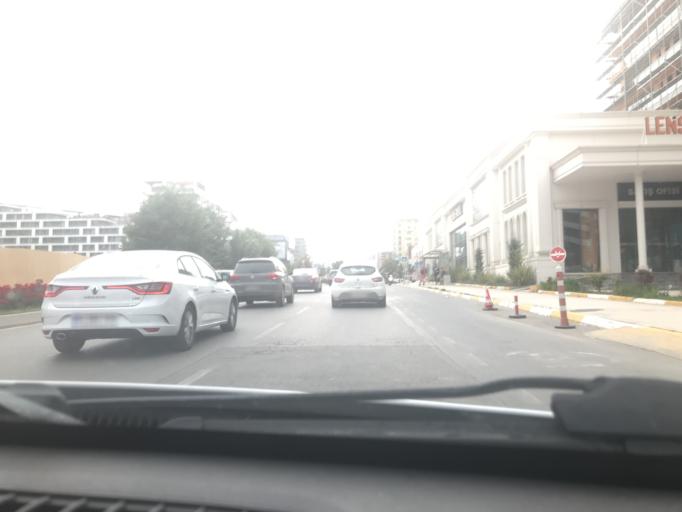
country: TR
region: Istanbul
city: Sultanbeyli
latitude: 40.9264
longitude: 29.3111
